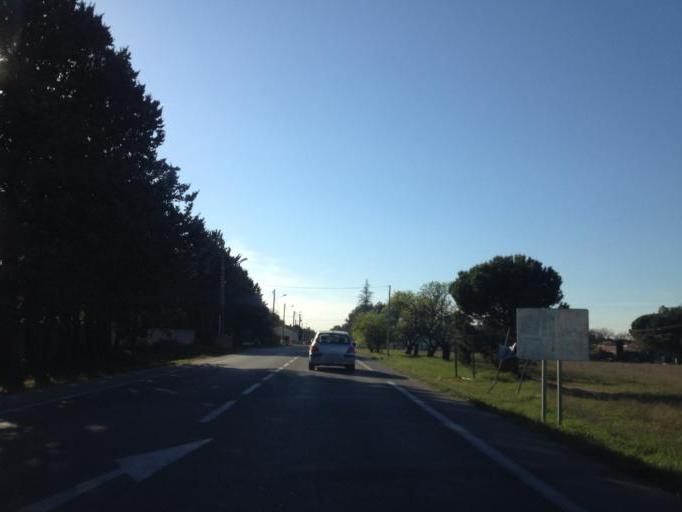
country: FR
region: Provence-Alpes-Cote d'Azur
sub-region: Departement des Bouches-du-Rhone
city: Saint-Cannat
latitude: 43.6171
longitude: 5.3122
